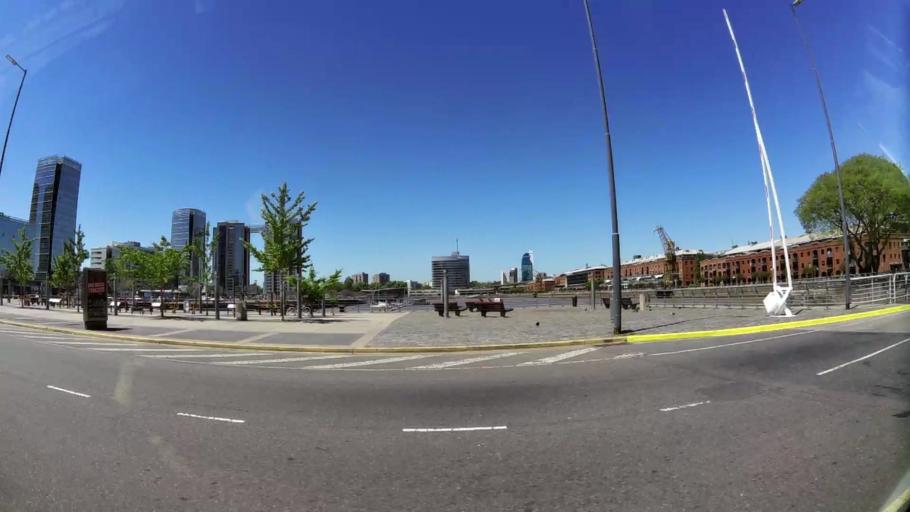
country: AR
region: Buenos Aires F.D.
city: Buenos Aires
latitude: -34.6179
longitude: -58.3638
